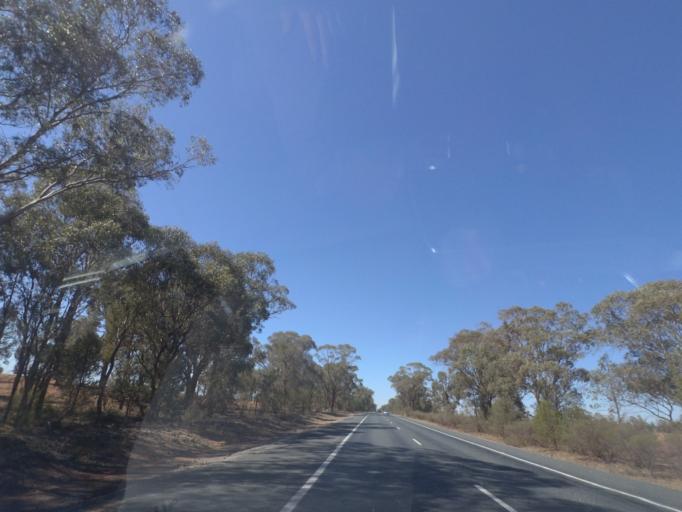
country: AU
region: New South Wales
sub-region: Bland
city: West Wyalong
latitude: -34.2112
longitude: 147.1087
